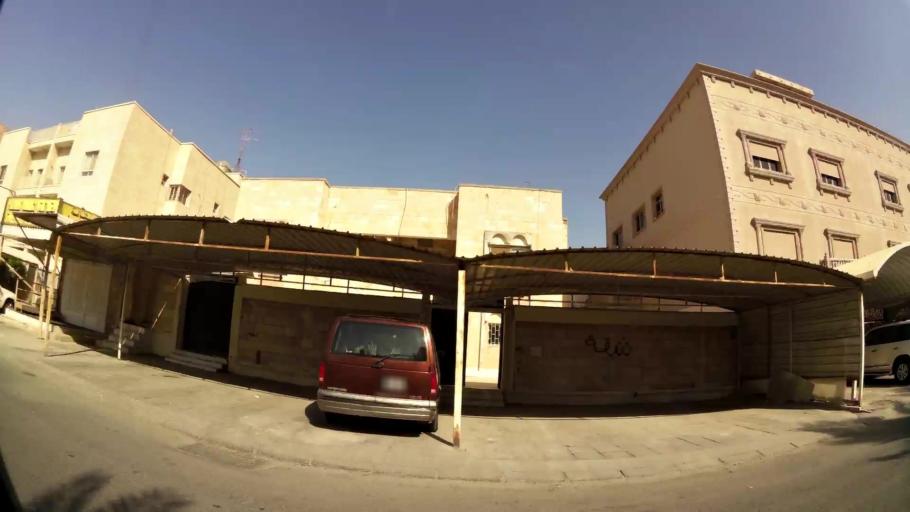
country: KW
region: Muhafazat Hawalli
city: Salwa
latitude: 29.2923
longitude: 48.0777
